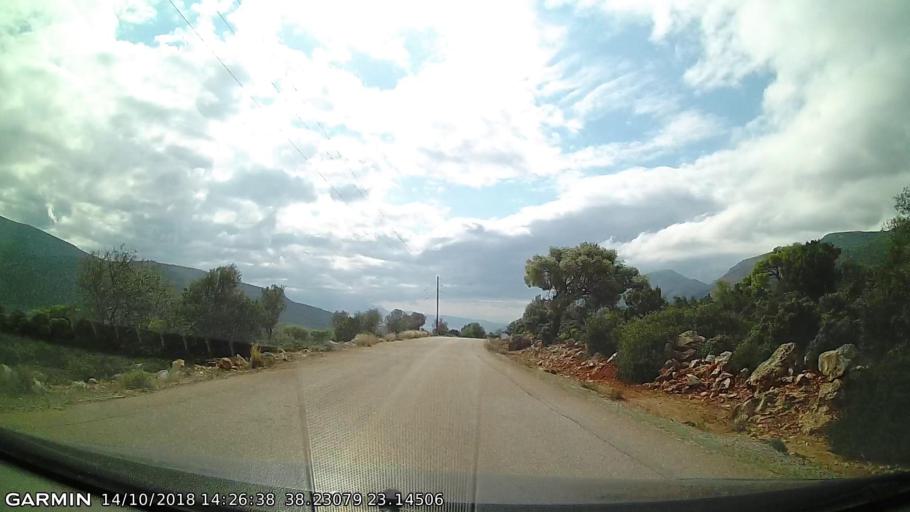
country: GR
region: Central Greece
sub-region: Nomos Voiotias
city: Kaparellion
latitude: 38.2307
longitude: 23.1449
